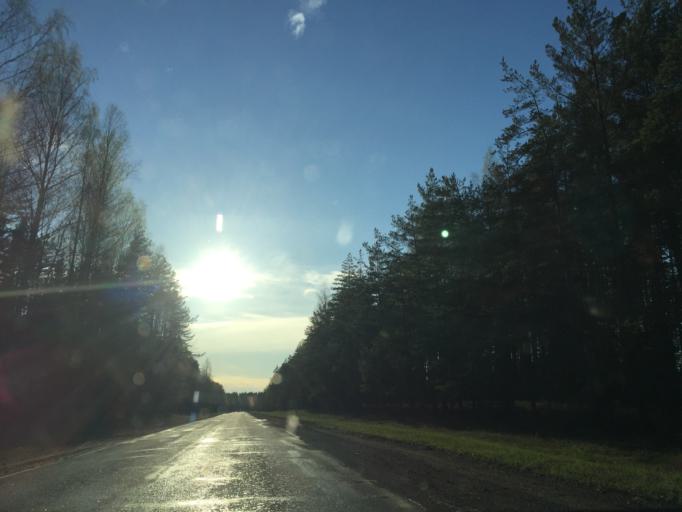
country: LV
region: Strenci
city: Seda
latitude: 57.6243
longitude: 25.7609
